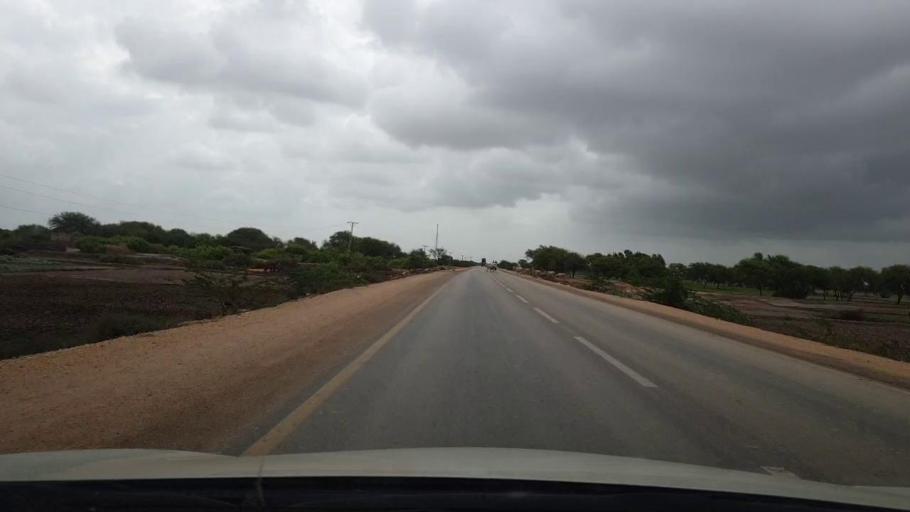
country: PK
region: Sindh
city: Mirpur Batoro
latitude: 24.6441
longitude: 68.4218
